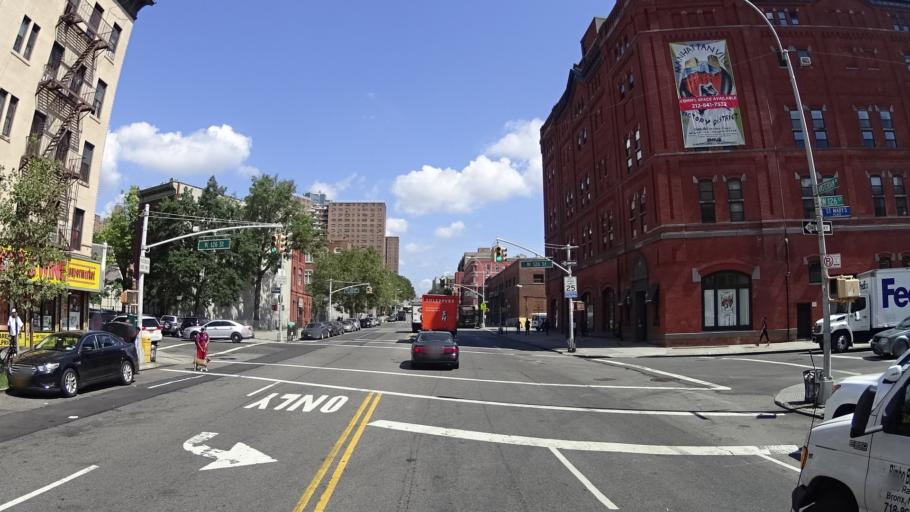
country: US
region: New Jersey
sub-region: Bergen County
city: Edgewater
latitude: 40.8139
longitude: -73.9559
